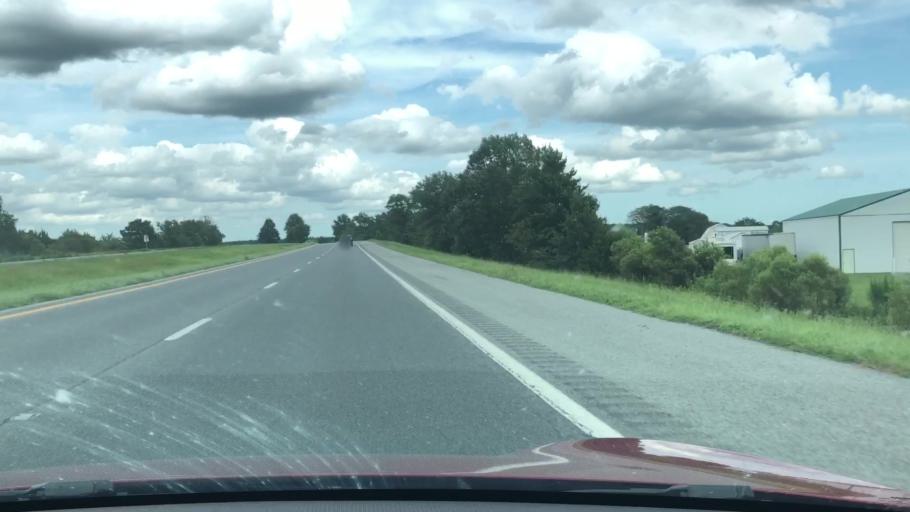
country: US
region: Maryland
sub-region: Wicomico County
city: Fruitland
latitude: 38.3039
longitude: -75.6169
